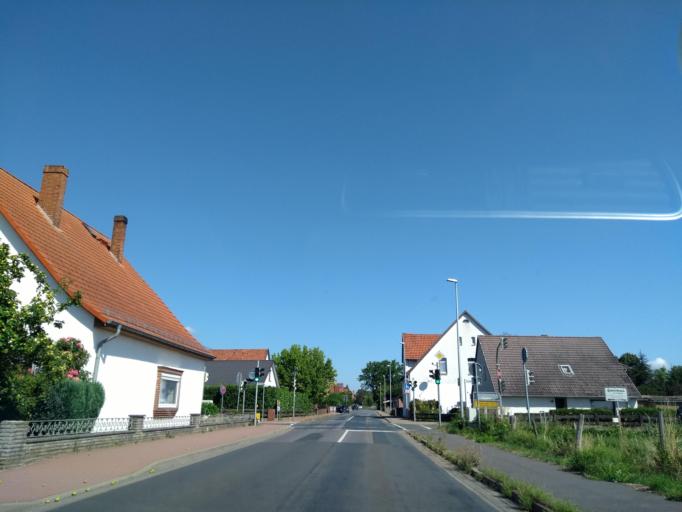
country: DE
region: Lower Saxony
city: Wunstorf
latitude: 52.4426
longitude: 9.4213
